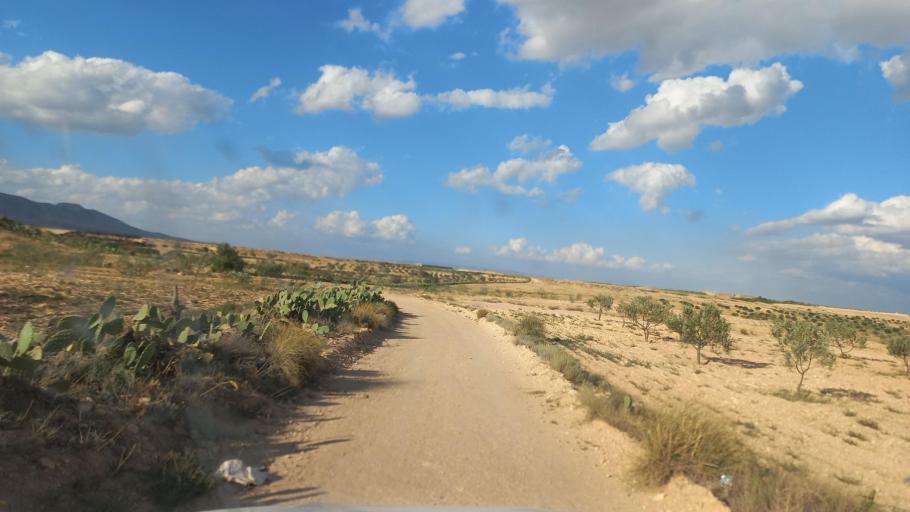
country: TN
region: Al Qasrayn
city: Sbiba
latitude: 35.3819
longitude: 9.0721
